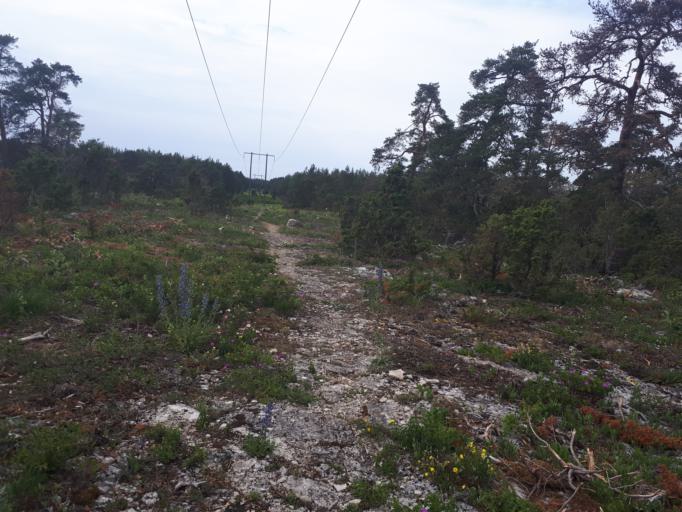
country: SE
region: Gotland
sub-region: Gotland
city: Visby
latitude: 57.6022
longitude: 18.3068
